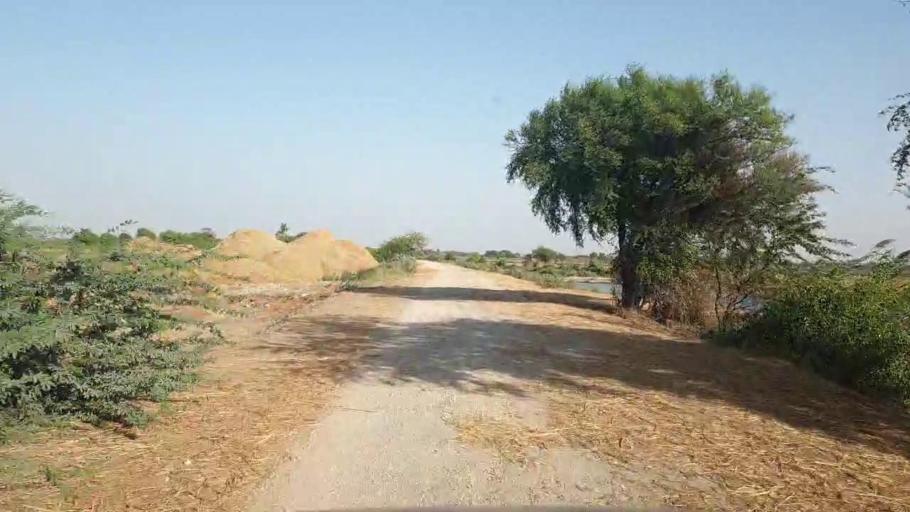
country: PK
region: Sindh
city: Rajo Khanani
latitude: 25.0033
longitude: 68.7529
